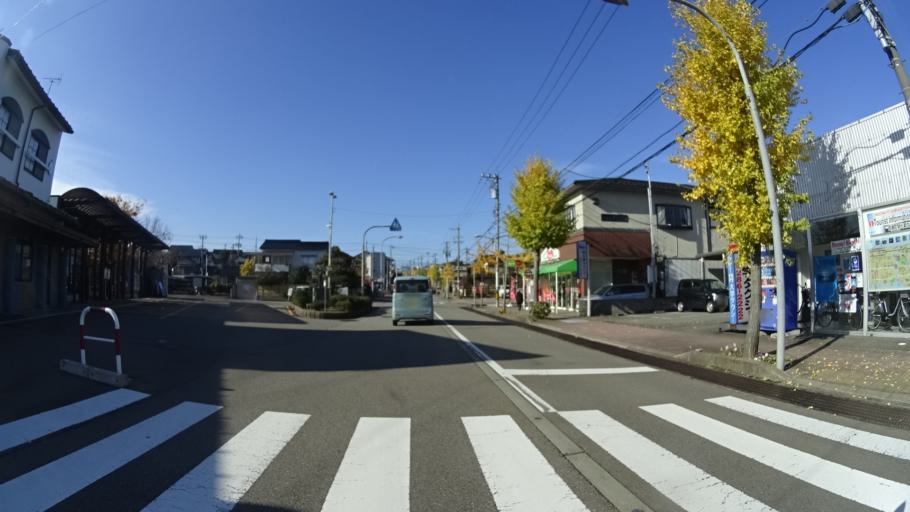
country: JP
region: Ishikawa
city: Kanazawa-shi
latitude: 36.6334
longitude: 136.6345
